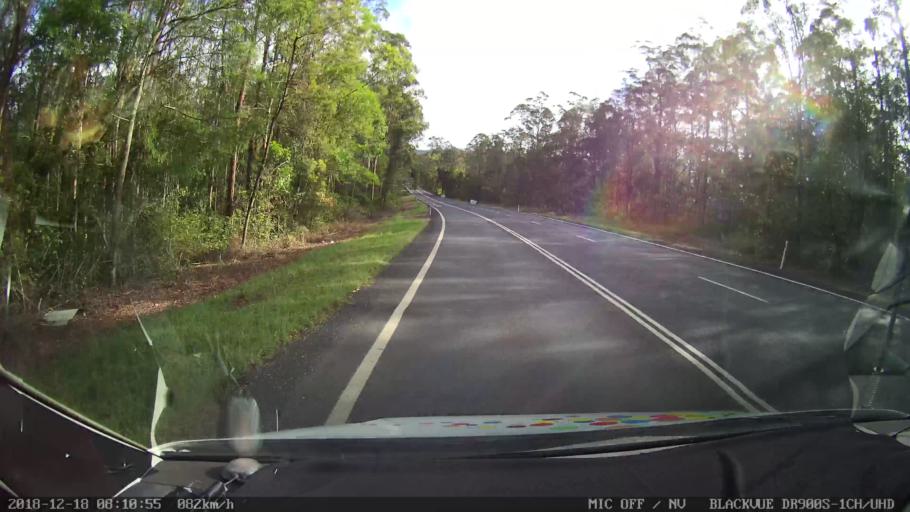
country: AU
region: New South Wales
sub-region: Kyogle
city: Kyogle
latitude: -28.3569
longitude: 152.6662
